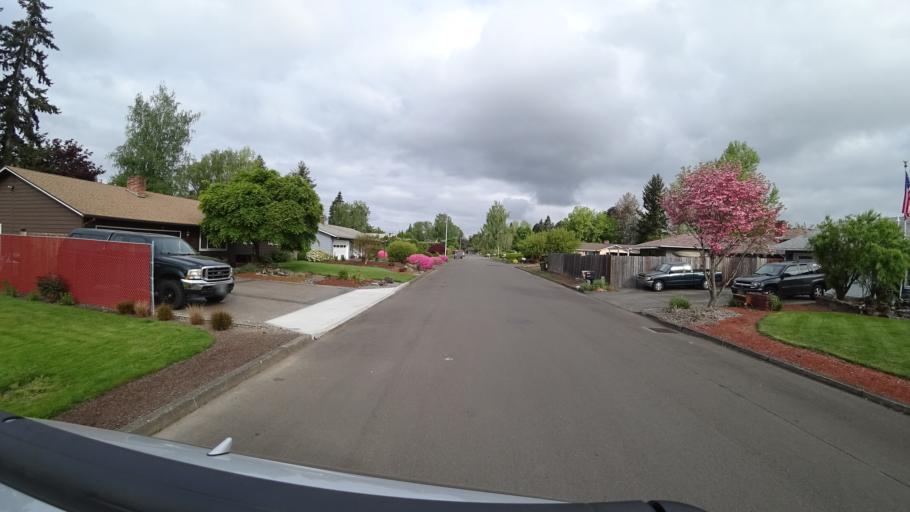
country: US
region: Oregon
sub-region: Washington County
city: Hillsboro
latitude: 45.5301
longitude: -122.9687
